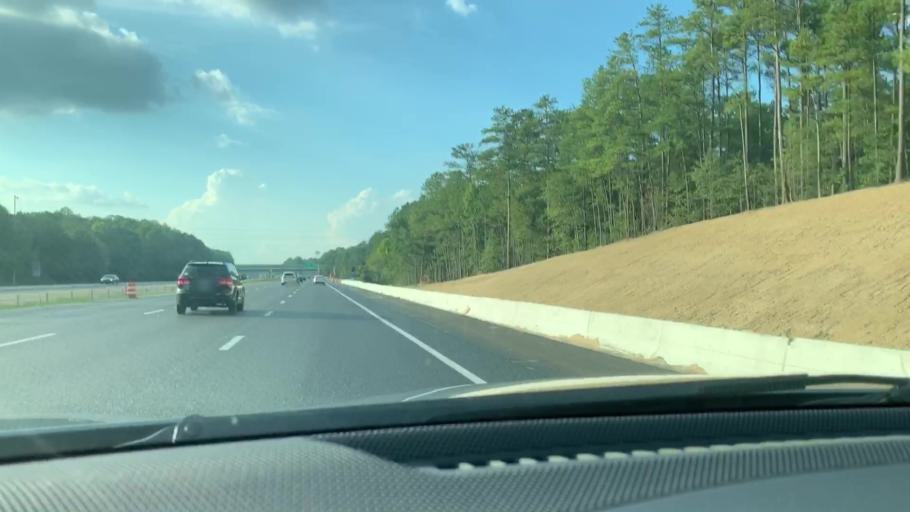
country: US
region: South Carolina
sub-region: Richland County
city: Woodfield
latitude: 34.0768
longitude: -80.9332
